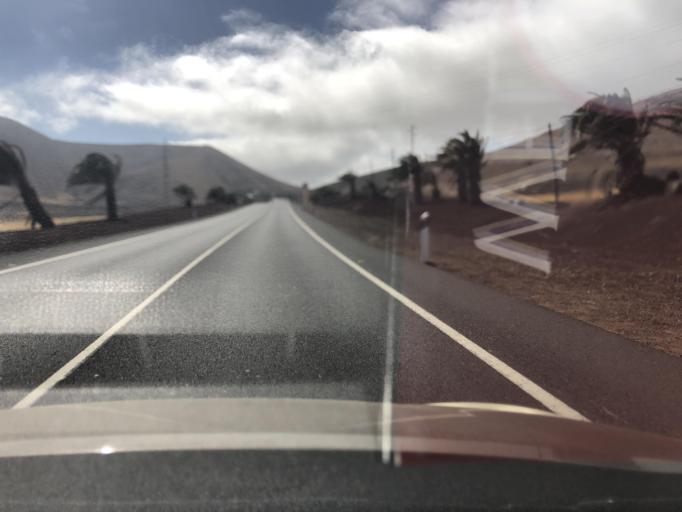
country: ES
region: Canary Islands
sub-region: Provincia de Las Palmas
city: Yaiza
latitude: 28.9370
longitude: -13.7321
